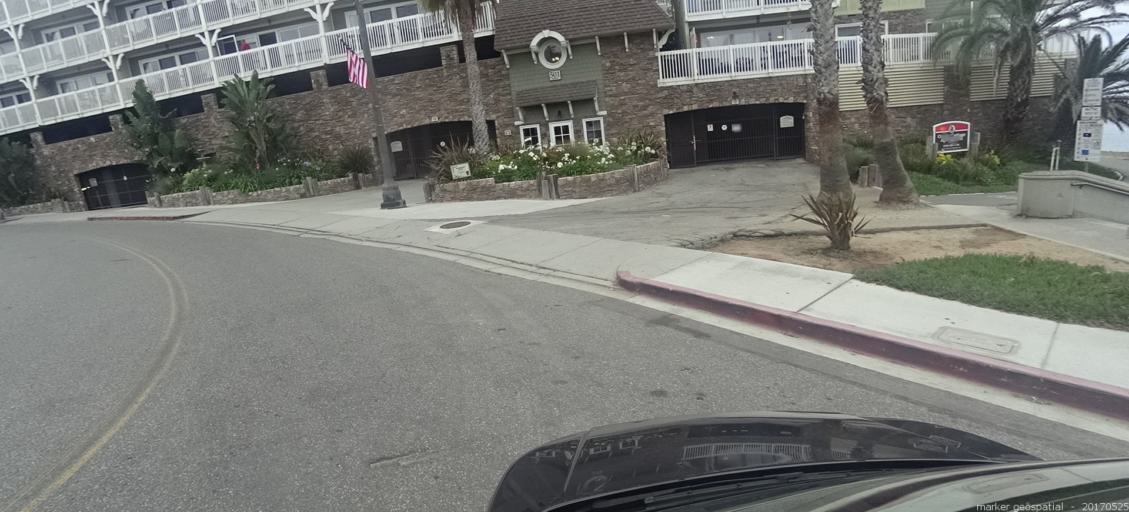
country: US
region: California
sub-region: Los Angeles County
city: Redondo Beach
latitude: 33.8363
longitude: -118.3896
